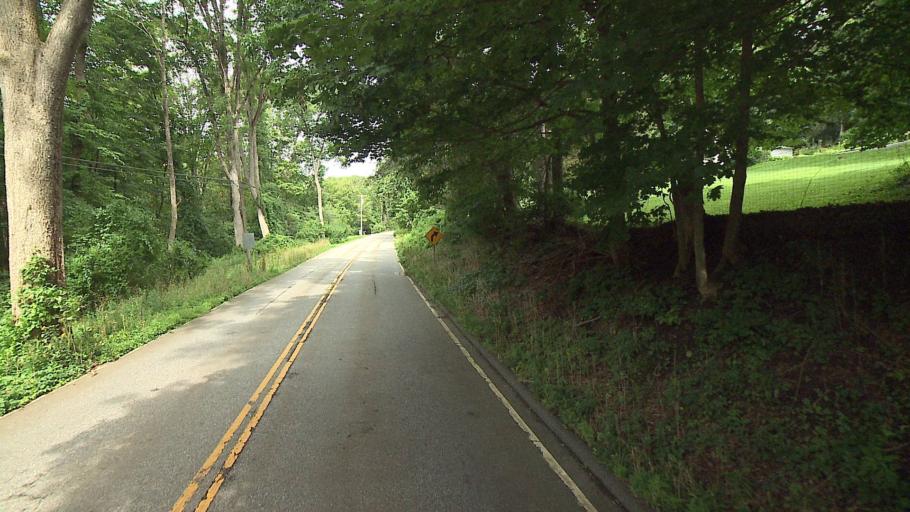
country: US
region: Connecticut
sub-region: Litchfield County
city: Kent
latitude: 41.7457
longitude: -73.5042
